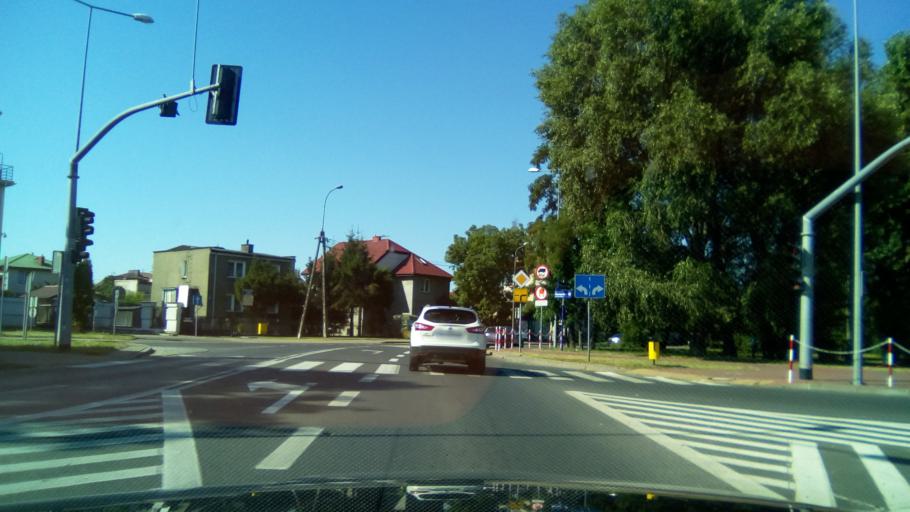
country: PL
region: Masovian Voivodeship
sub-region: Plock
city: Plock
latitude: 52.5391
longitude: 19.7328
